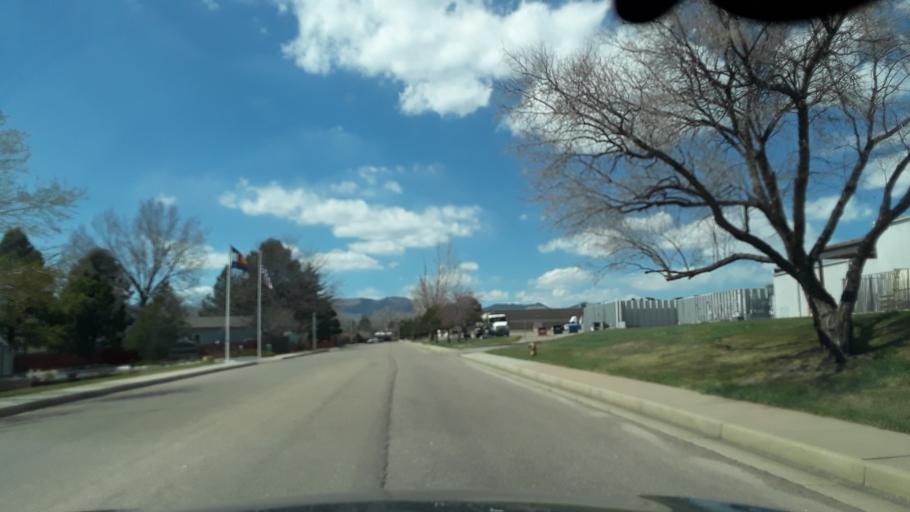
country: US
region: Colorado
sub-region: El Paso County
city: Colorado Springs
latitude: 38.9032
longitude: -104.7780
